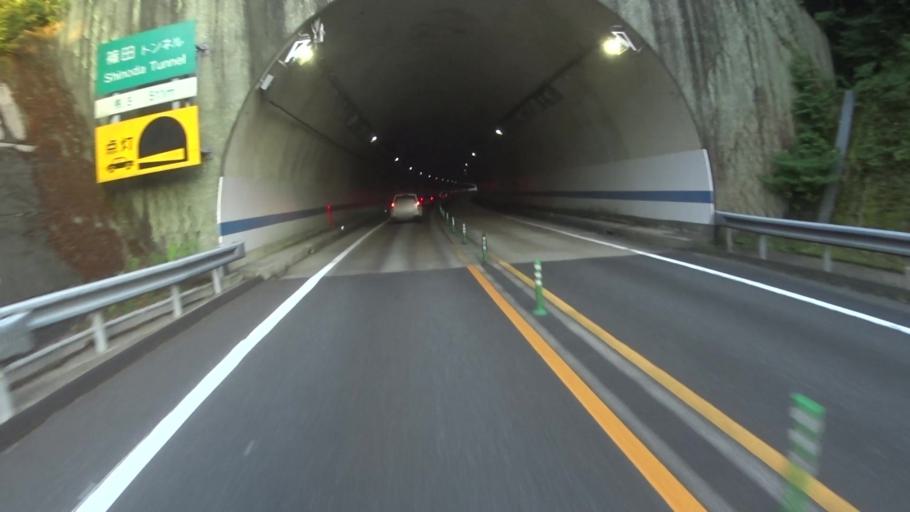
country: JP
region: Kyoto
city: Ayabe
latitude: 35.3743
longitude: 135.2738
